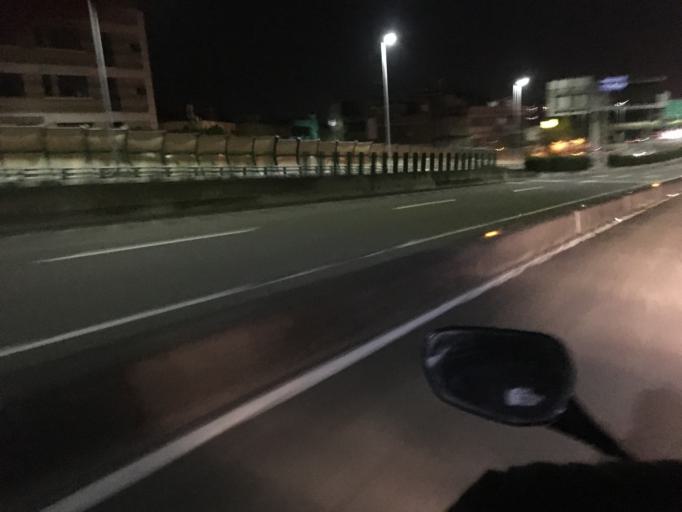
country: TW
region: Taiwan
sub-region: Hsinchu
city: Hsinchu
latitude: 24.7964
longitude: 120.9488
